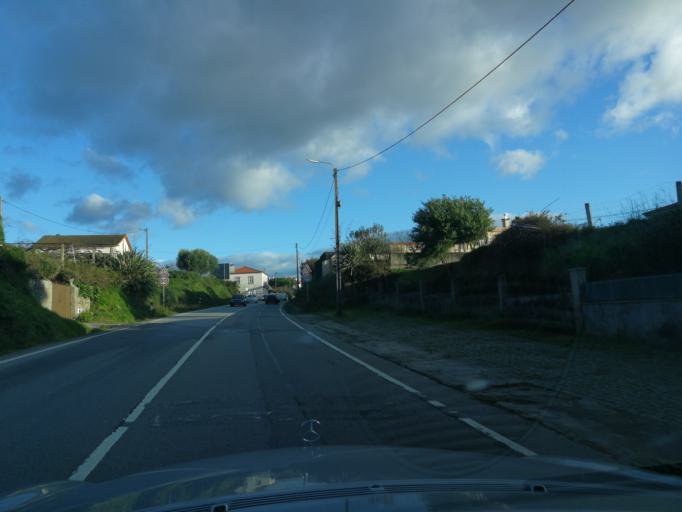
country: PT
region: Braga
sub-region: Esposende
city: Marinhas
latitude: 41.6152
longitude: -8.7464
